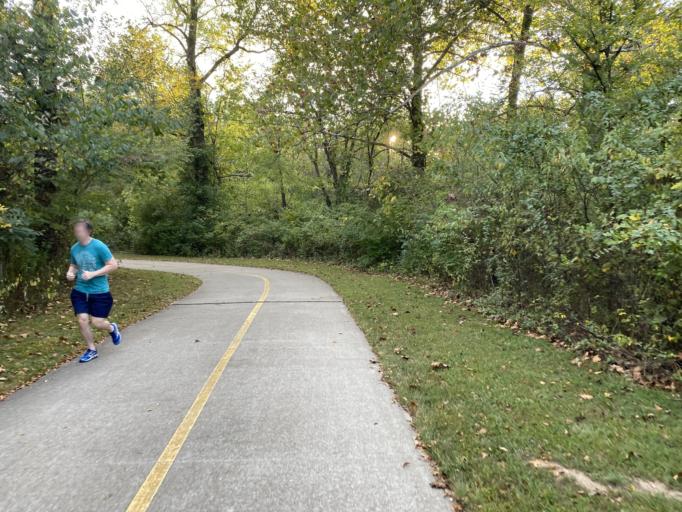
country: US
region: Arkansas
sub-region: Washington County
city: Johnson
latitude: 36.0986
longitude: -94.2177
